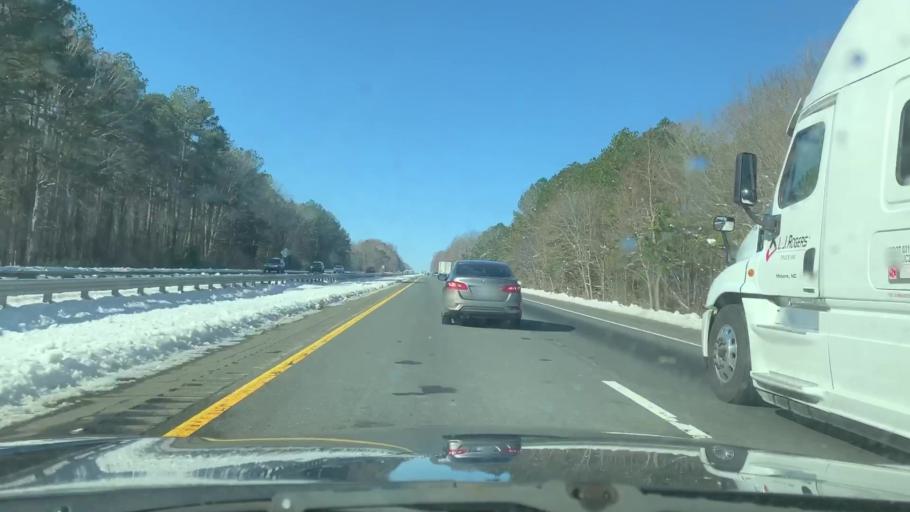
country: US
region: North Carolina
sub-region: Orange County
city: Hillsborough
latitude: 36.0423
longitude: -79.0337
